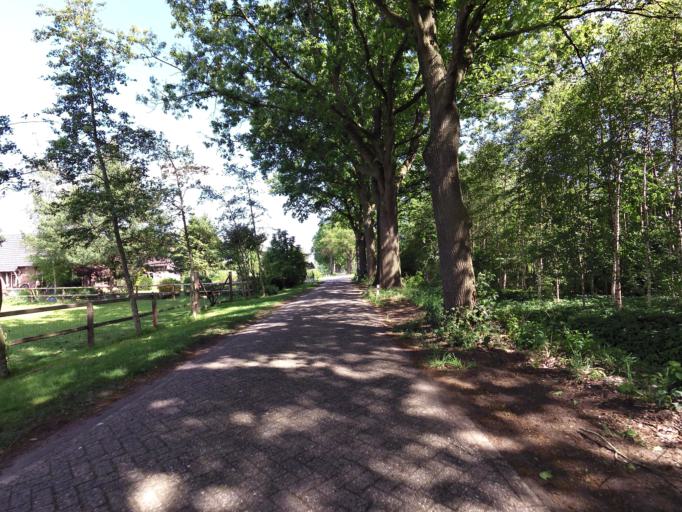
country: NL
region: Gelderland
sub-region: Gemeente Bronckhorst
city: Zelhem
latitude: 51.9964
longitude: 6.3889
